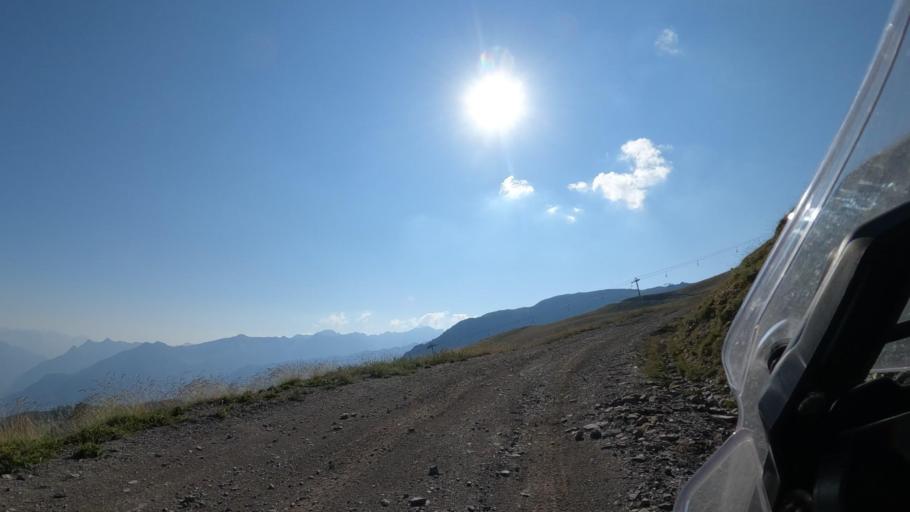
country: FR
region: Provence-Alpes-Cote d'Azur
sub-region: Departement des Hautes-Alpes
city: Guillestre
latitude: 44.6017
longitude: 6.6289
